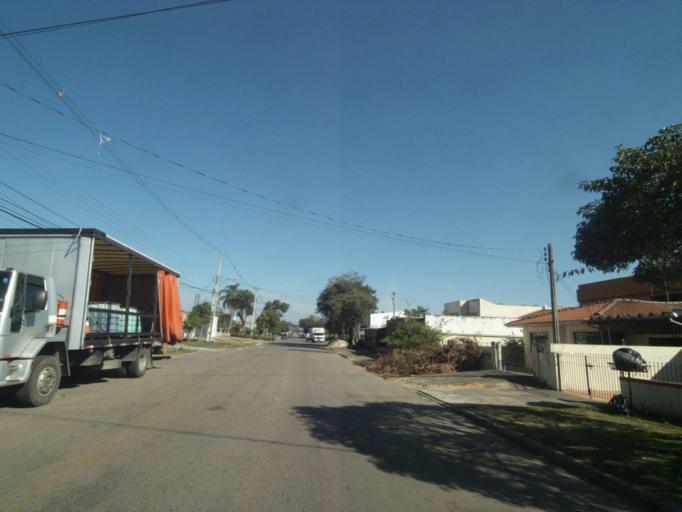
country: BR
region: Parana
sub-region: Sao Jose Dos Pinhais
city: Sao Jose dos Pinhais
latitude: -25.4881
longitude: -49.2358
